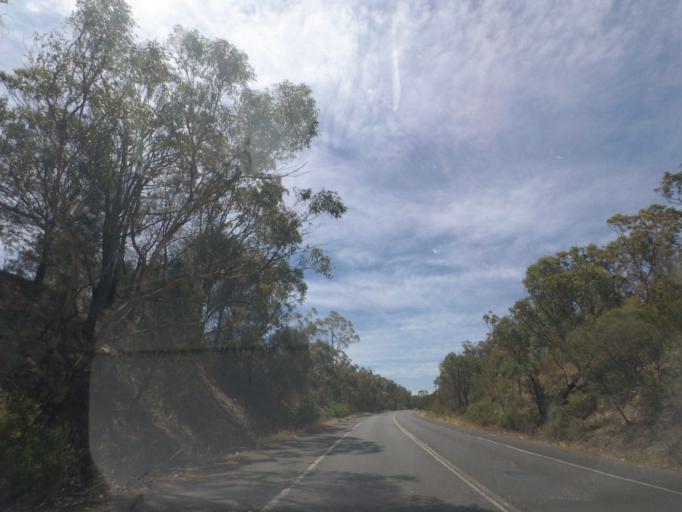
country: AU
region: New South Wales
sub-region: Wollondilly
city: Buxton
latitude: -34.2650
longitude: 150.5730
